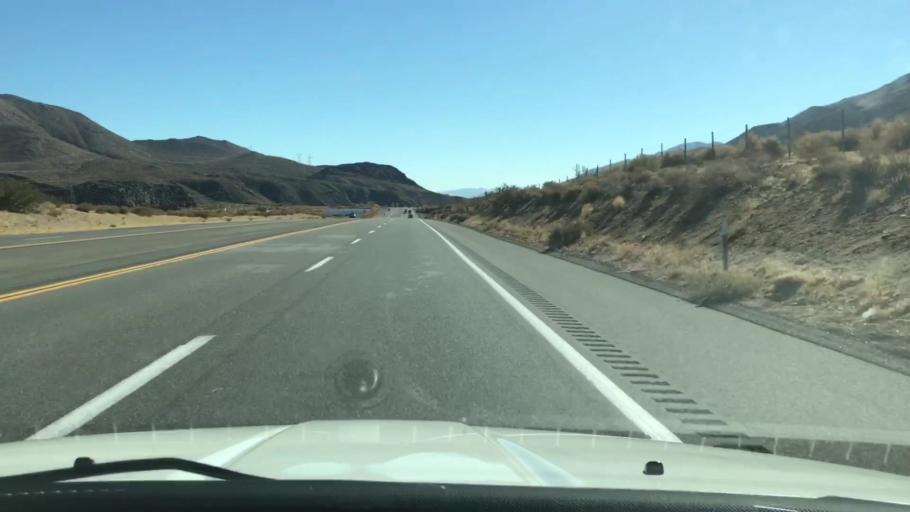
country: US
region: California
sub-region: Kern County
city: Inyokern
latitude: 35.9488
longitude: -117.9090
